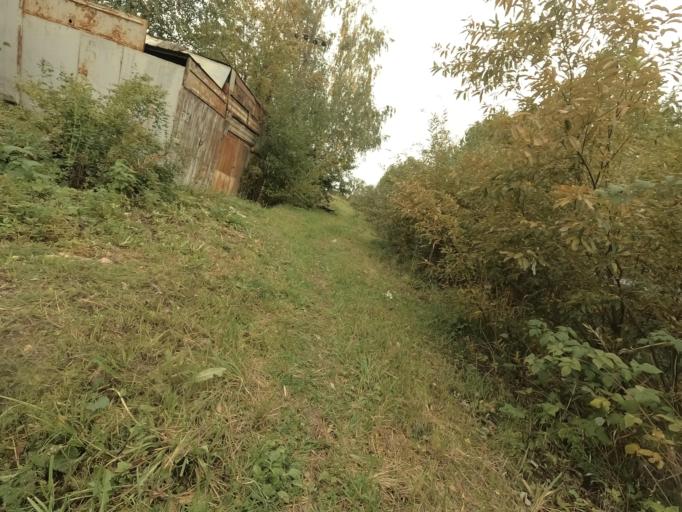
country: RU
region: Leningrad
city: Rybatskoye
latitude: 59.8354
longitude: 30.4923
